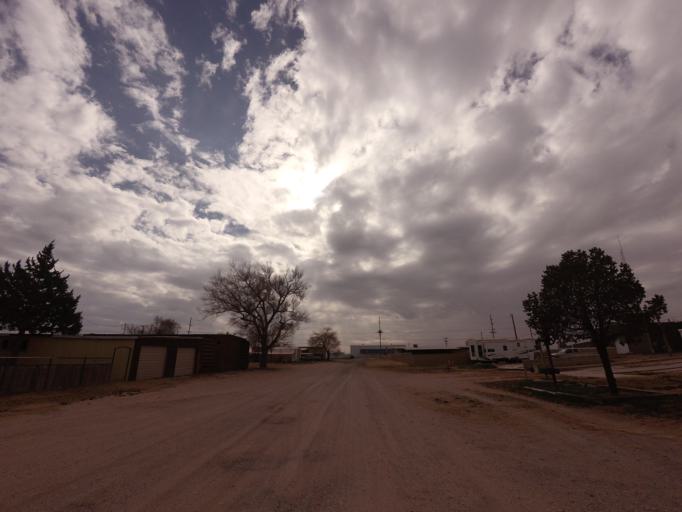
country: US
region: New Mexico
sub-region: Curry County
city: Clovis
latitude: 34.3912
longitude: -103.2155
